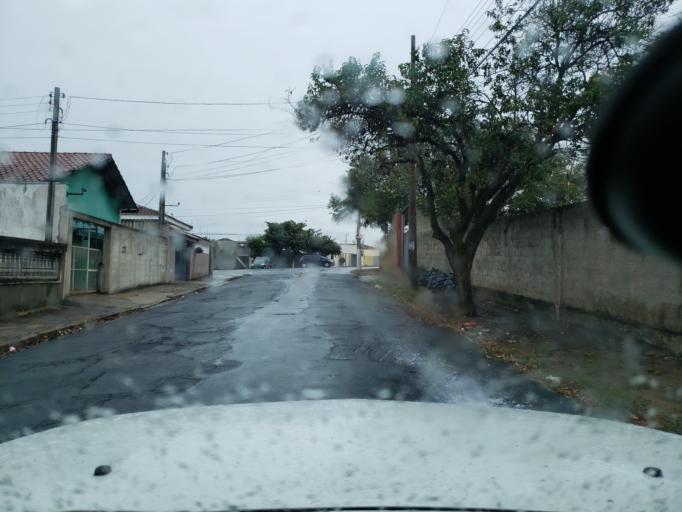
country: BR
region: Sao Paulo
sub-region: Moji-Guacu
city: Mogi-Gaucu
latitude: -22.3793
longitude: -46.9360
